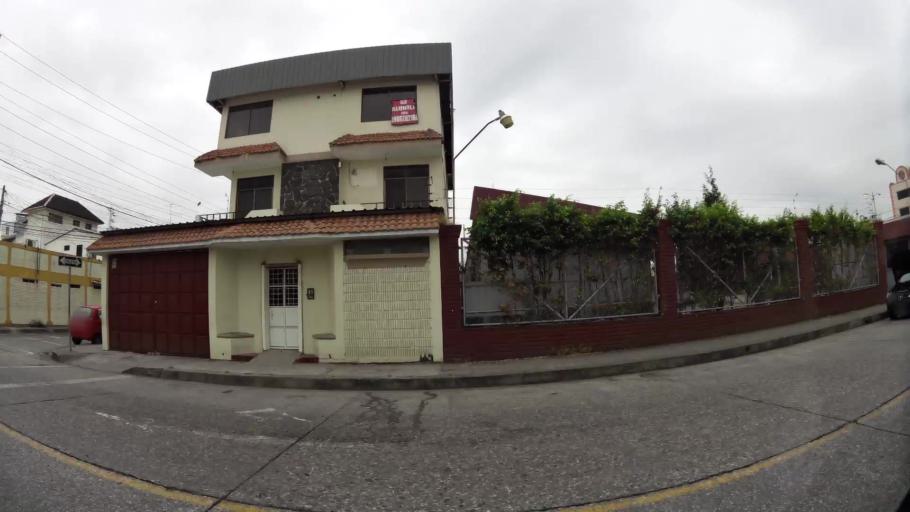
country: EC
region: Guayas
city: Eloy Alfaro
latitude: -2.1525
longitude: -79.8935
